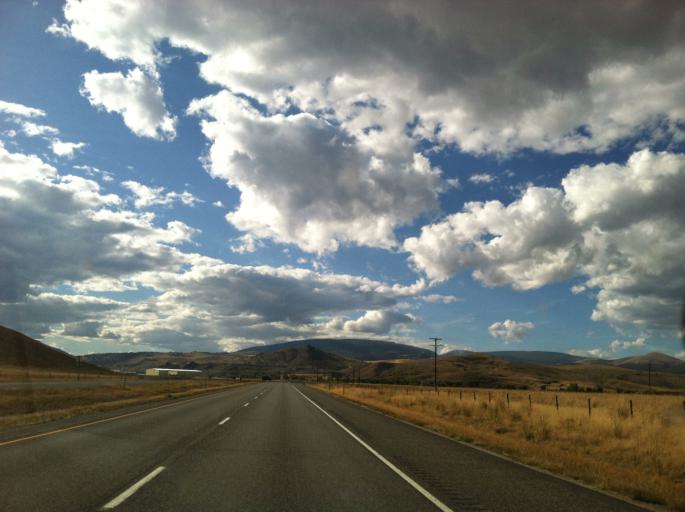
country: US
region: Montana
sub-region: Deer Lodge County
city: Anaconda
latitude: 46.1262
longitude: -112.8920
